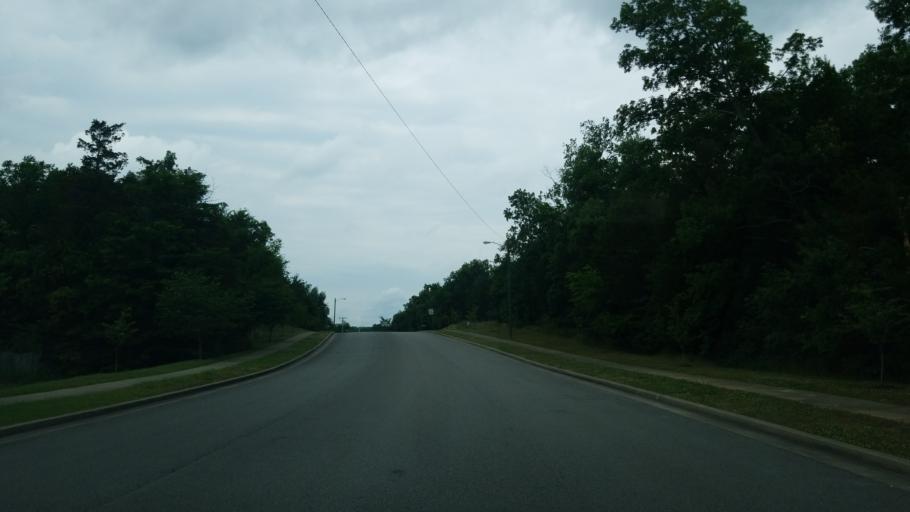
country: US
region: Tennessee
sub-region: Rutherford County
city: La Vergne
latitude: 36.0699
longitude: -86.5861
